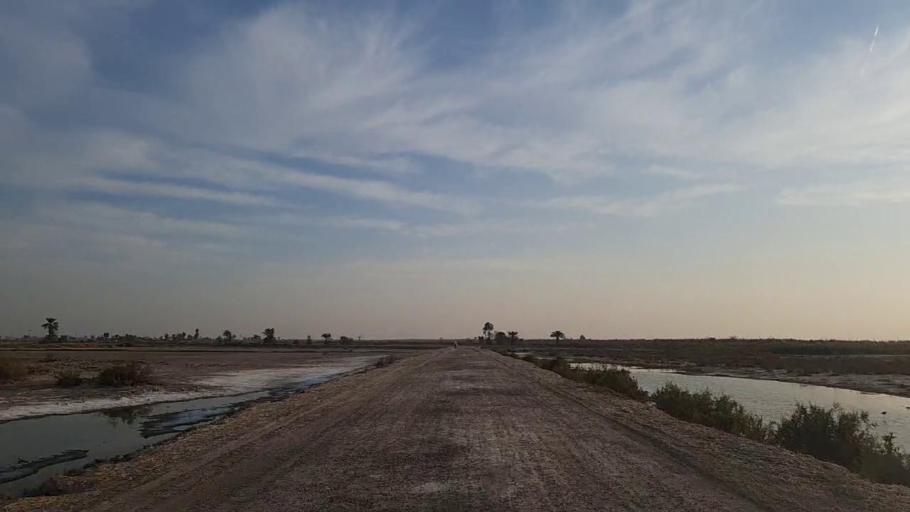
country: PK
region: Sindh
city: Bandhi
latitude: 26.5804
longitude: 68.3336
